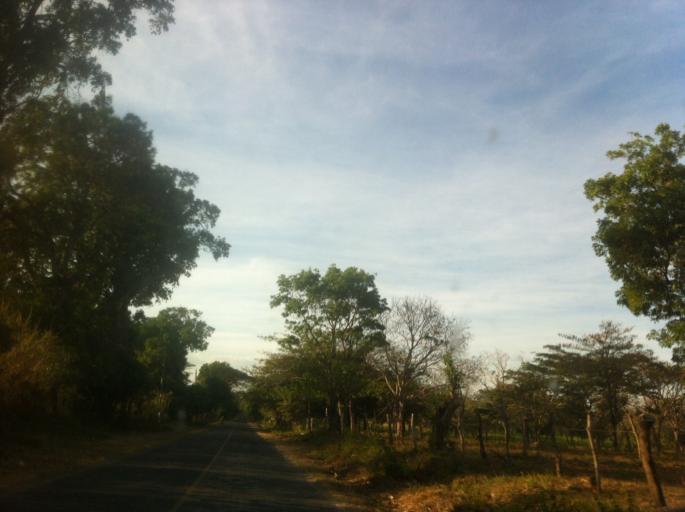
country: NI
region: Rivas
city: Buenos Aires
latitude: 11.4633
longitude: -85.8440
